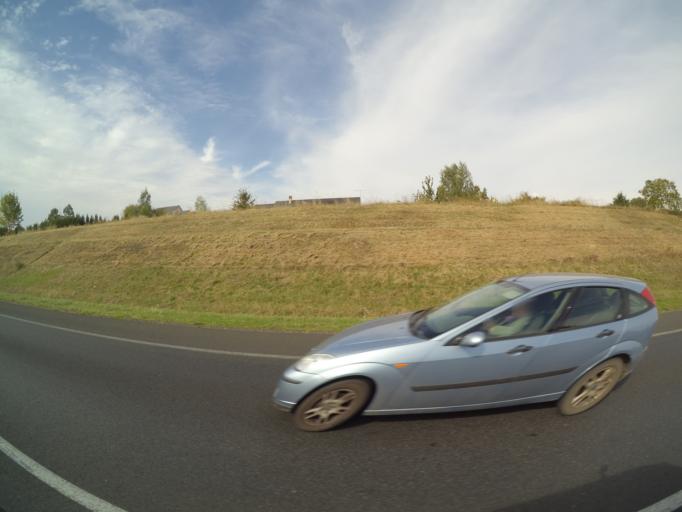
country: FR
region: Pays de la Loire
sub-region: Departement de Maine-et-Loire
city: Distre
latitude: 47.2472
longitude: -0.1055
